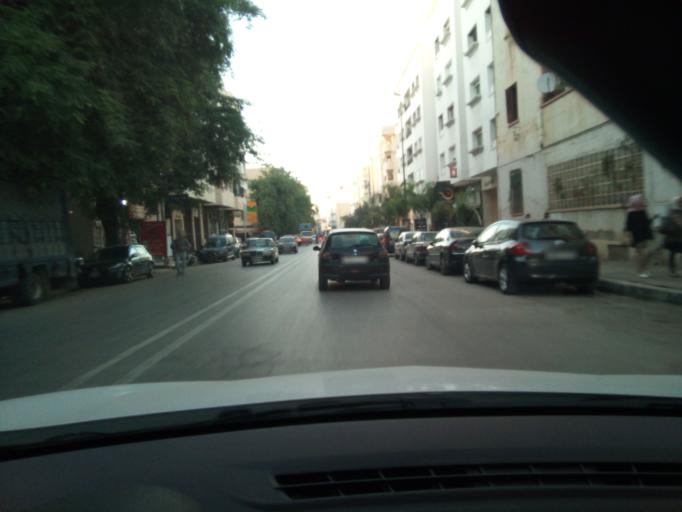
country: MA
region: Fes-Boulemane
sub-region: Fes
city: Fes
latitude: 34.0299
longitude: -4.9929
